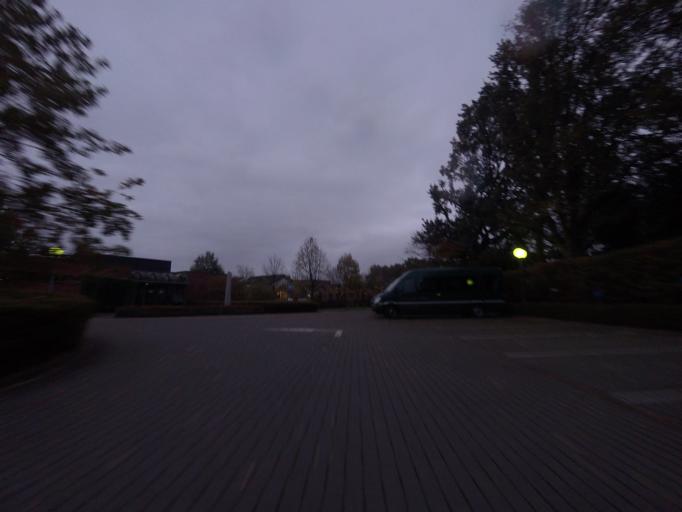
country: BE
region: Flanders
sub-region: Provincie Antwerpen
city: Bonheiden
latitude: 51.0193
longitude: 4.5422
